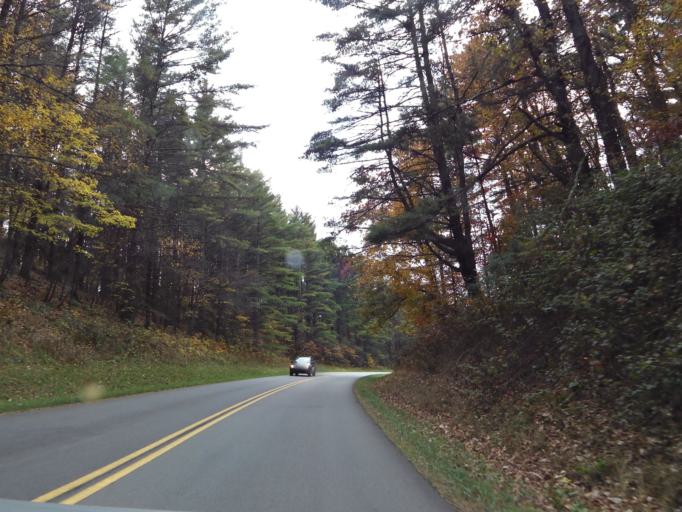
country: US
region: North Carolina
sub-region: Ashe County
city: Jefferson
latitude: 36.3681
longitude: -81.3502
